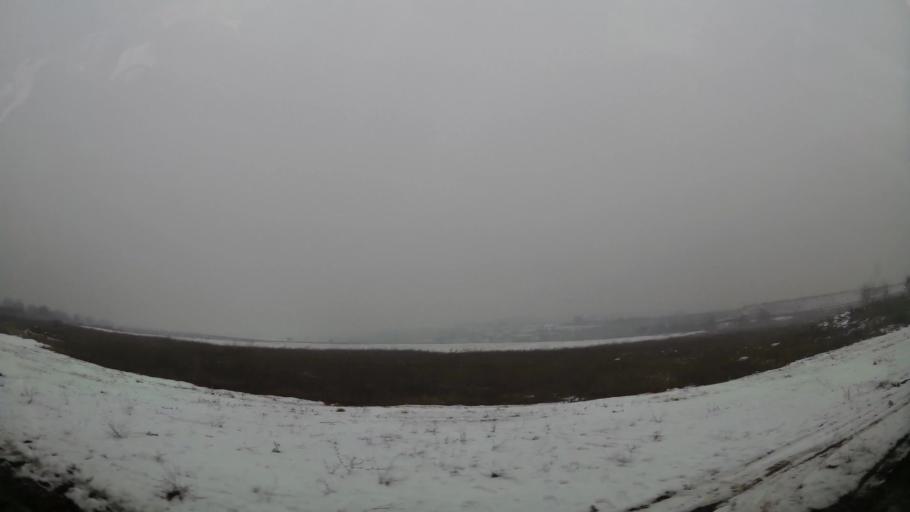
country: MK
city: Miladinovci
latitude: 41.9613
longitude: 21.6299
